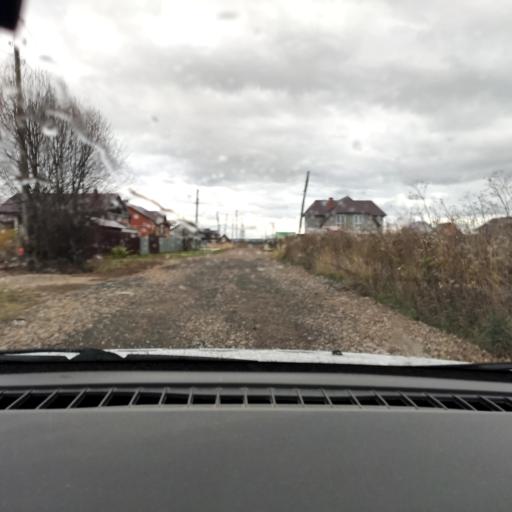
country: RU
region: Perm
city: Kultayevo
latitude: 57.8976
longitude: 55.9556
